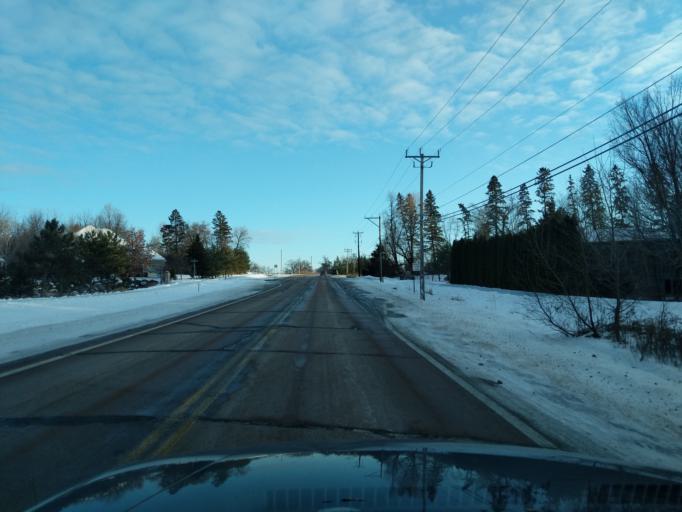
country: US
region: Minnesota
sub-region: Carver County
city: Victoria
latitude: 44.8718
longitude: -93.6389
